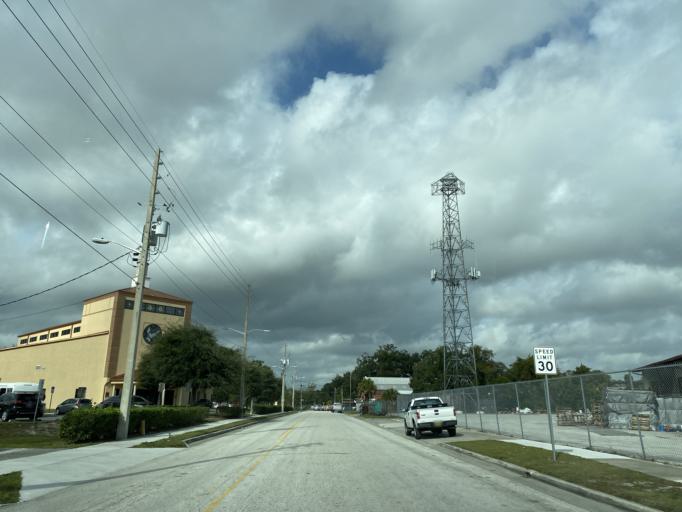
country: US
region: Florida
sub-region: Orange County
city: Orlando
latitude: 28.5423
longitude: -81.4059
